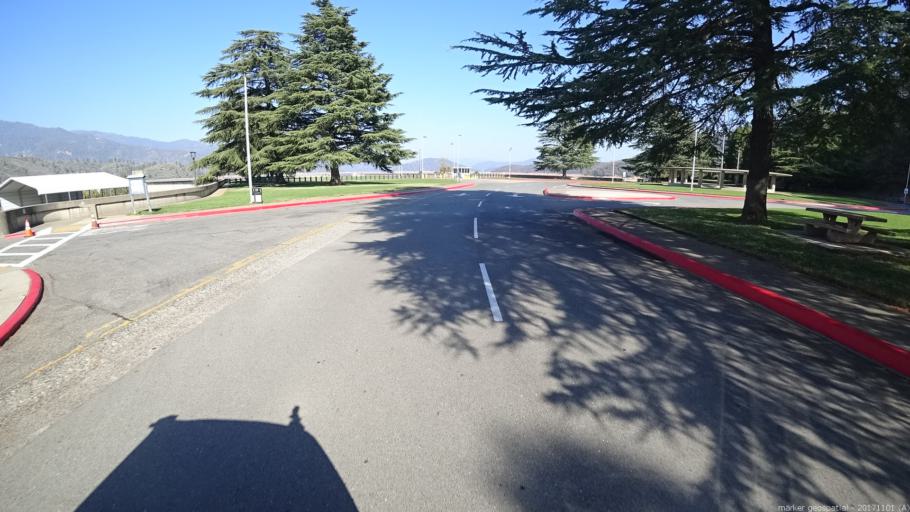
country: US
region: California
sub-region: Shasta County
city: Central Valley (historical)
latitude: 40.7142
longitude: -122.4160
